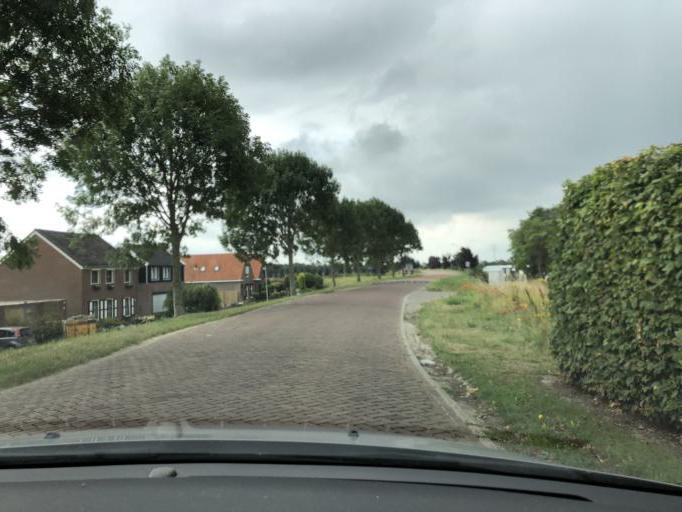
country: NL
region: Zeeland
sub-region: Gemeente Reimerswaal
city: Yerseke
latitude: 51.4427
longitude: 4.0806
